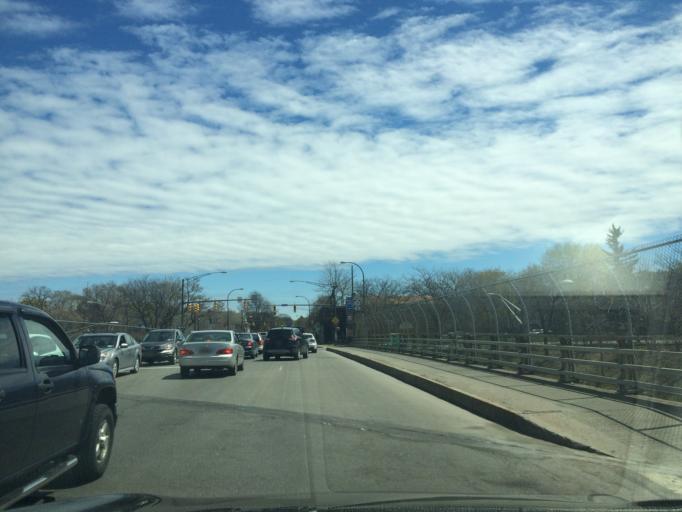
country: US
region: New York
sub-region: Monroe County
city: Rochester
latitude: 43.1424
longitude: -77.5866
